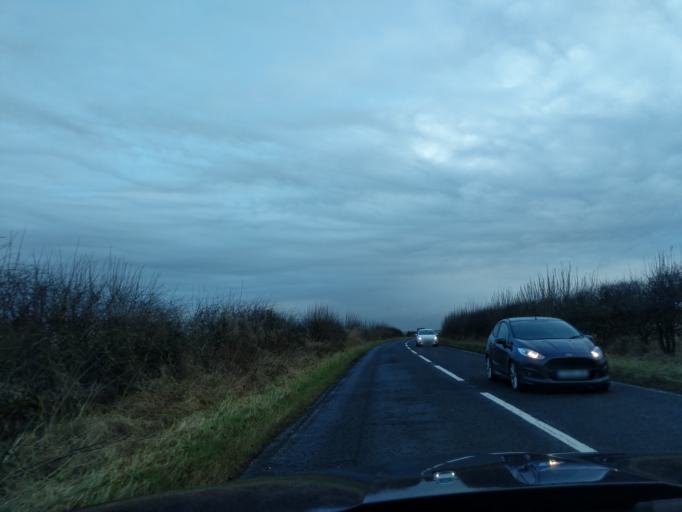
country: GB
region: England
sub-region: Northumberland
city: Rothley
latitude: 55.1333
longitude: -1.9620
